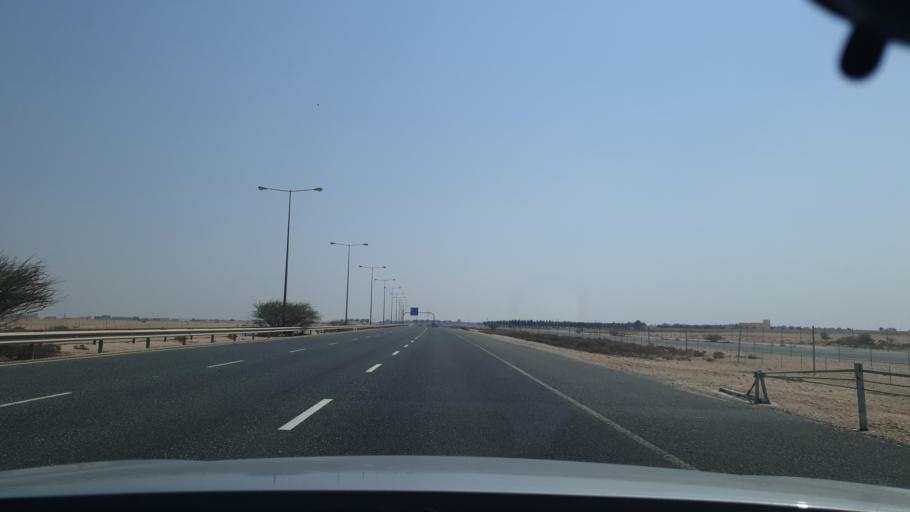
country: QA
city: Al Ghuwayriyah
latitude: 25.7953
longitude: 51.3873
